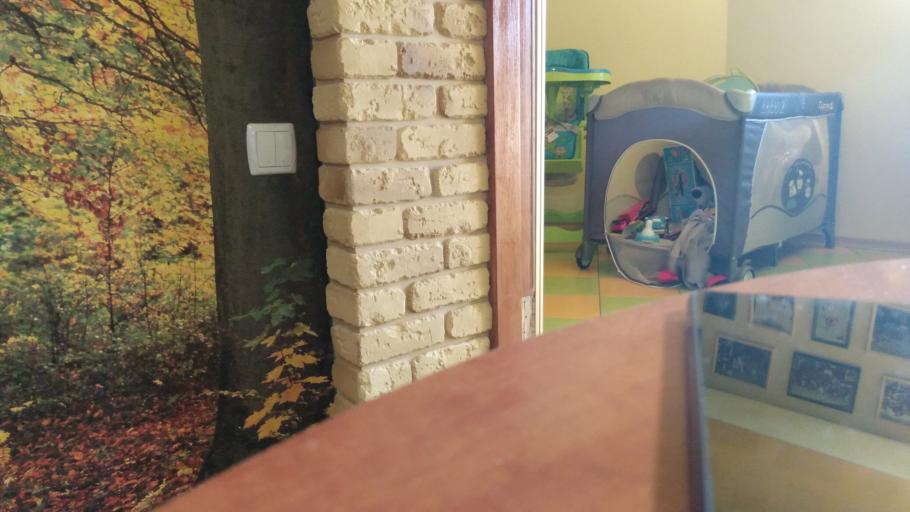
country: RU
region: Tverskaya
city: Bologoye
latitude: 57.9050
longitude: 34.2468
